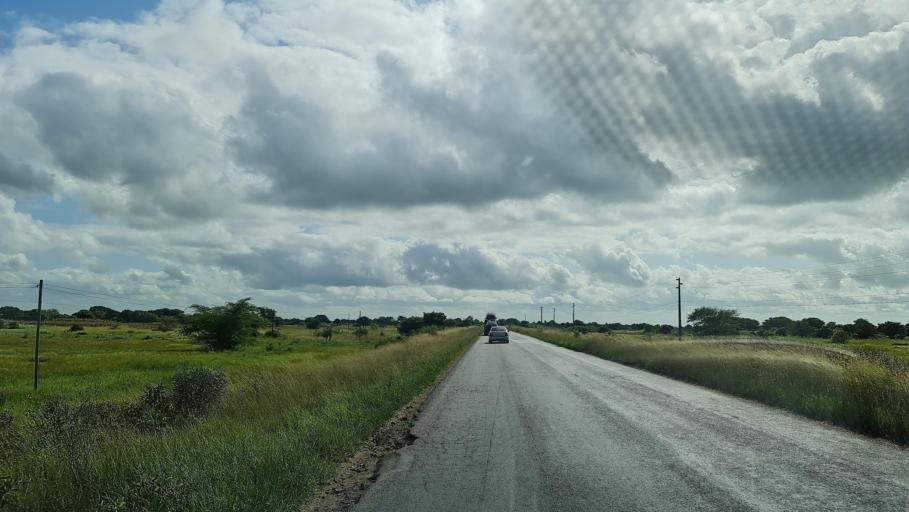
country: MZ
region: Gaza
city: Macia
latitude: -25.0923
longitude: 32.8371
